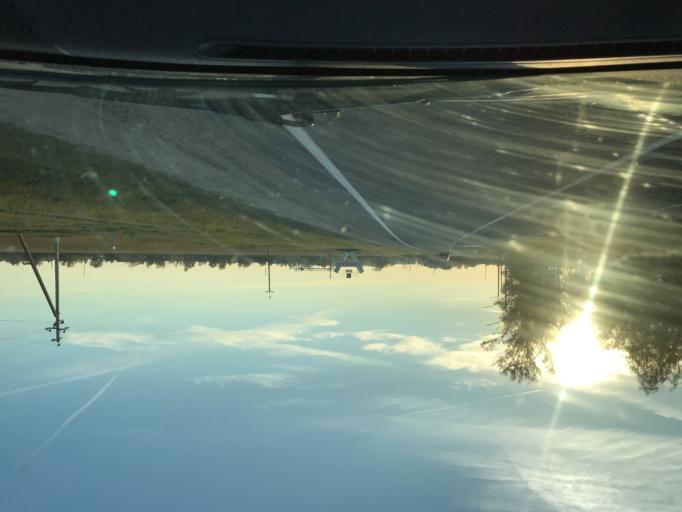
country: BY
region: Brest
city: Horad Kobryn
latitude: 52.2172
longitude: 24.4062
